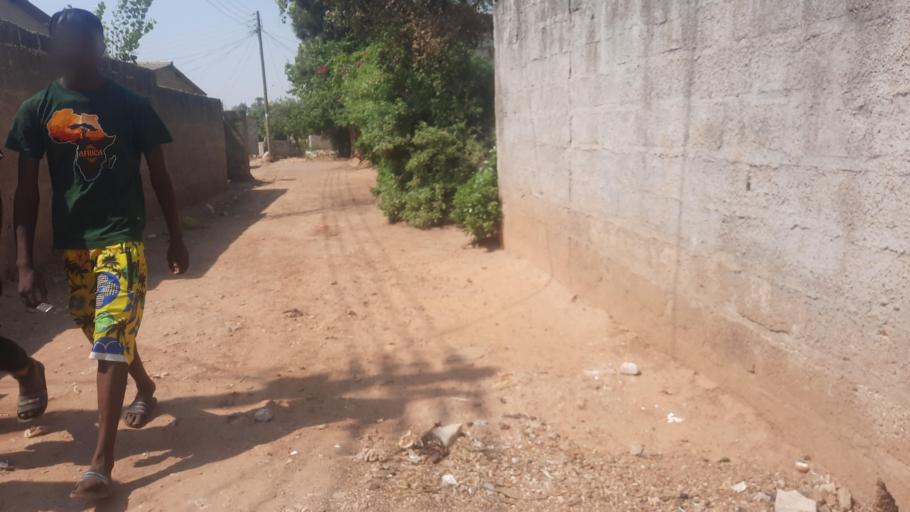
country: ZM
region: Lusaka
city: Lusaka
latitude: -15.3973
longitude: 28.3769
